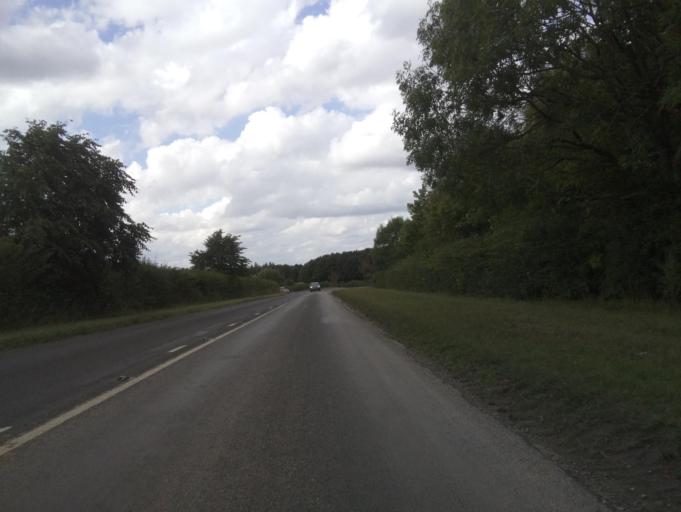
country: GB
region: England
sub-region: North Yorkshire
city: Ripon
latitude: 54.1789
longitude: -1.5573
